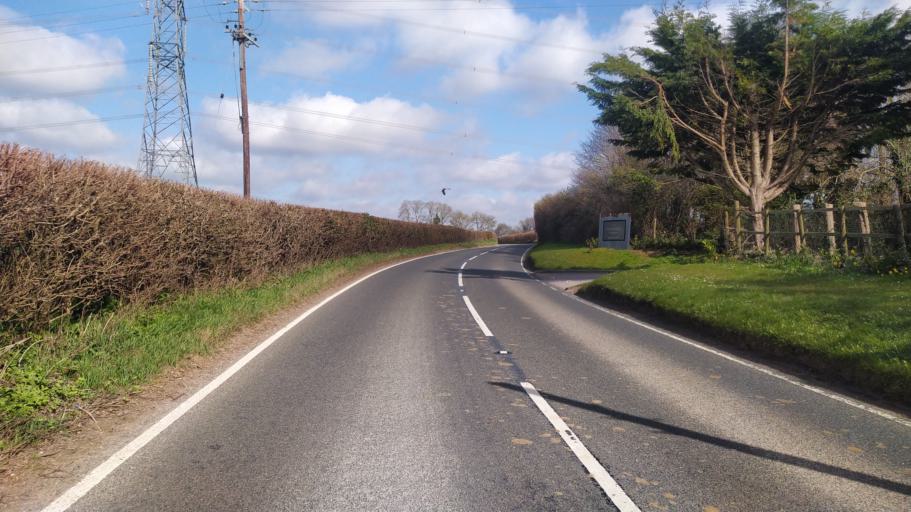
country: GB
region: England
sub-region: Dorset
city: Bridport
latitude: 50.7557
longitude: -2.7381
